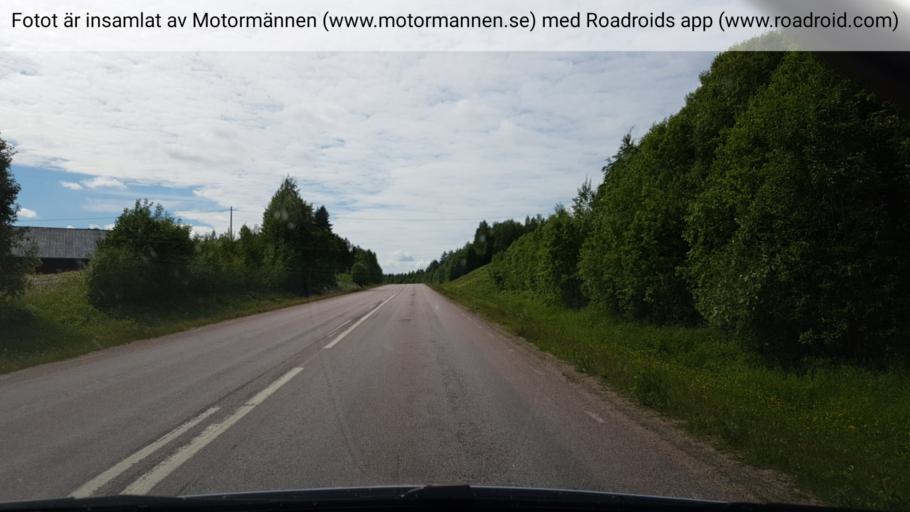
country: SE
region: Norrbotten
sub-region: Overtornea Kommun
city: OEvertornea
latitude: 66.4535
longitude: 23.6231
